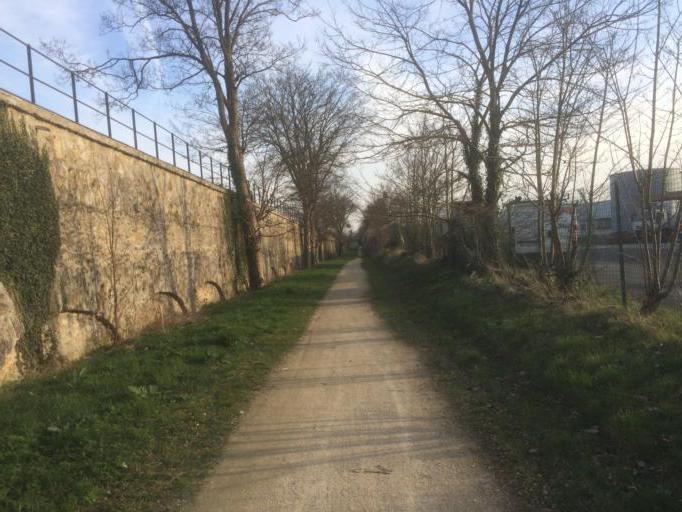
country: FR
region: Ile-de-France
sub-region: Departement de l'Essonne
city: Morsang-sur-Orge
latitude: 48.6648
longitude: 2.3718
